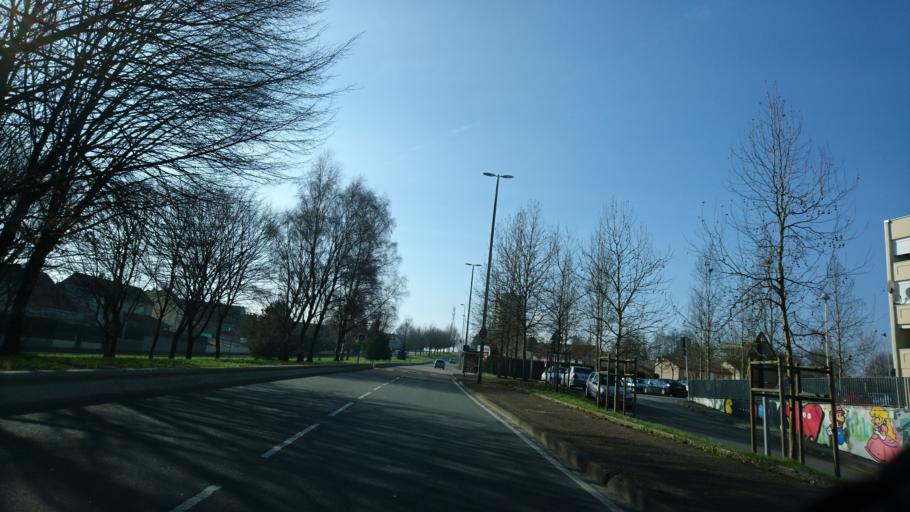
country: FR
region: Limousin
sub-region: Departement de la Haute-Vienne
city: Le Palais-sur-Vienne
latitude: 45.8763
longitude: 1.3009
